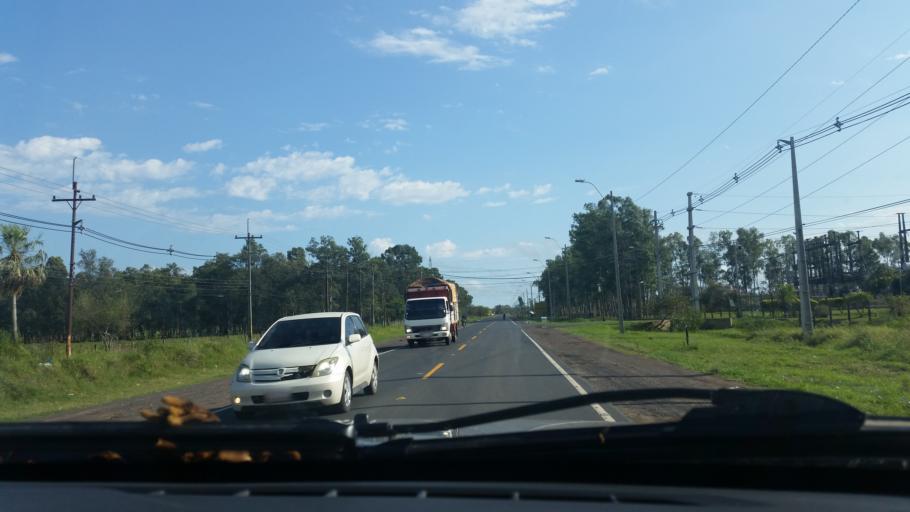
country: PY
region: Presidente Hayes
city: Villa Hayes
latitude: -25.0742
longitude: -57.5316
